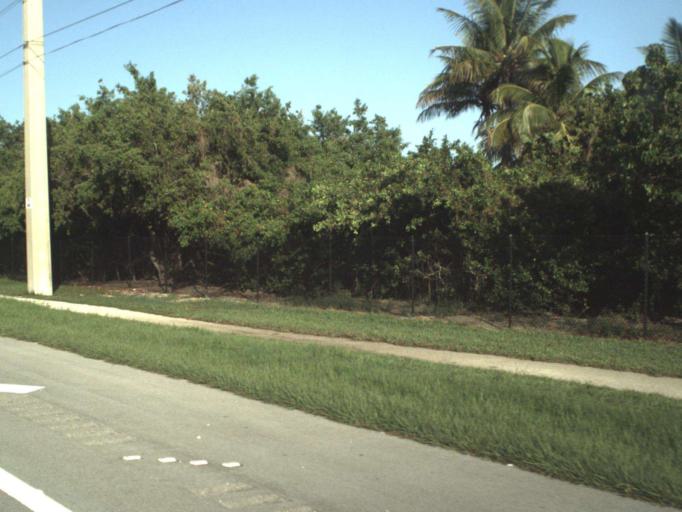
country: US
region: Florida
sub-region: Monroe County
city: Islamorada
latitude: 24.8073
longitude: -80.8388
